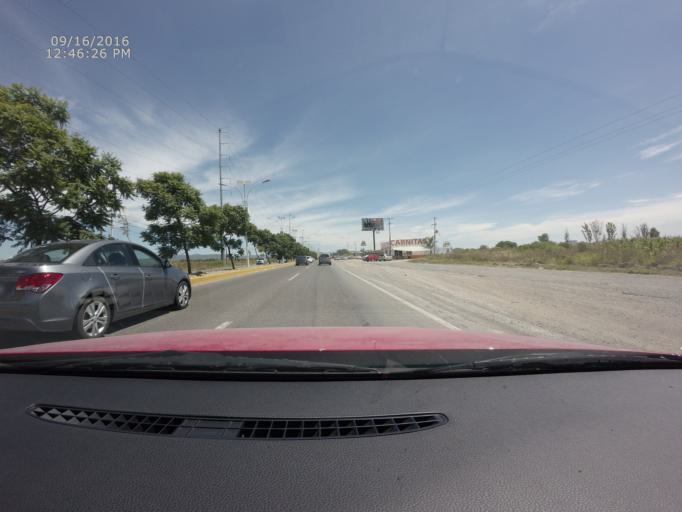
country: MX
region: Queretaro
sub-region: El Marques
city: La Loma
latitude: 20.5927
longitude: -100.1828
